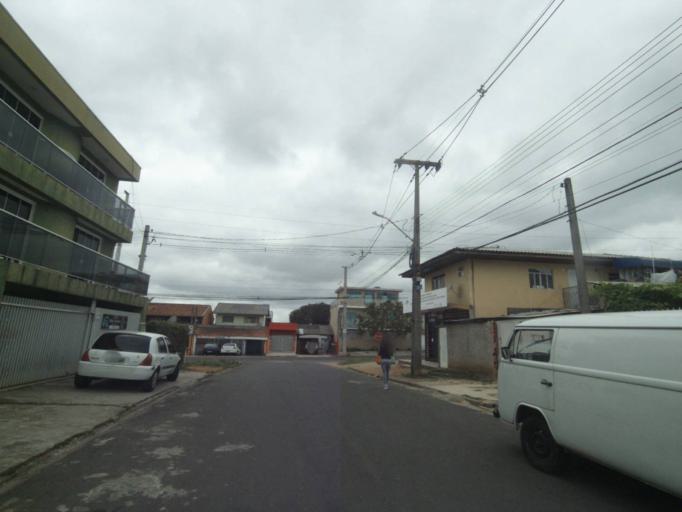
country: BR
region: Parana
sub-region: Sao Jose Dos Pinhais
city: Sao Jose dos Pinhais
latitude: -25.5554
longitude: -49.2551
